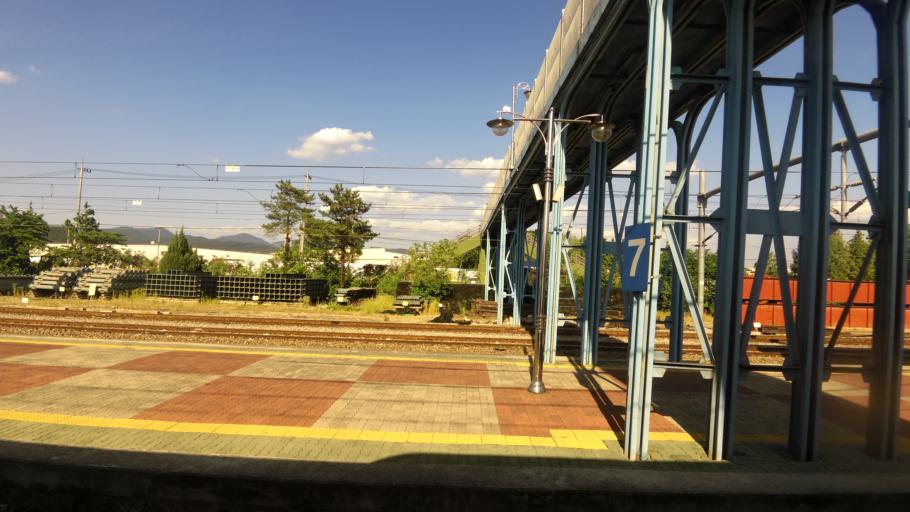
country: KR
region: Gyeongsangbuk-do
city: Waegwan
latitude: 35.9927
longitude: 128.4005
